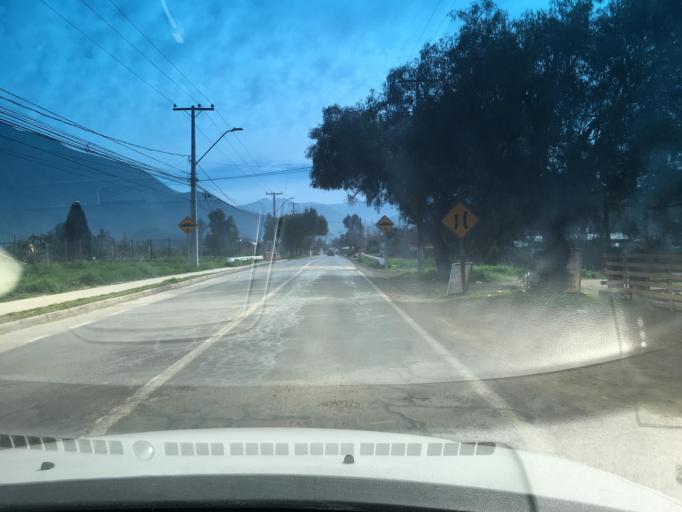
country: CL
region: Santiago Metropolitan
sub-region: Provincia de Chacabuco
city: Lampa
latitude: -33.0892
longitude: -70.9289
